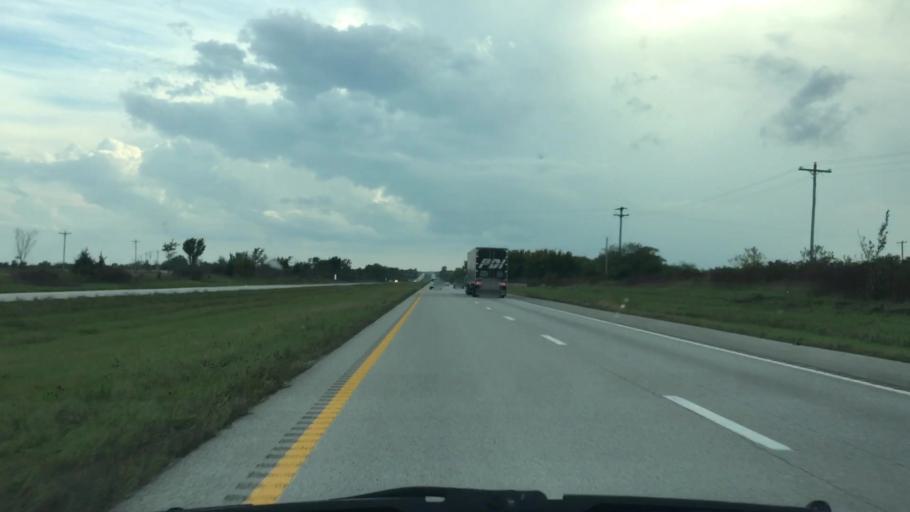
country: US
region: Missouri
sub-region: Clinton County
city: Cameron
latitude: 39.8328
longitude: -94.1860
